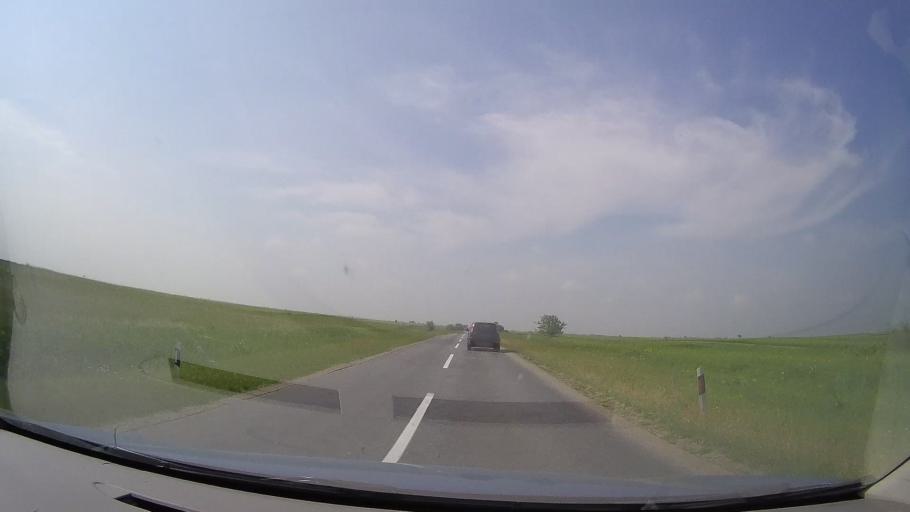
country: RS
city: Padina
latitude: 45.1611
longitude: 20.7504
